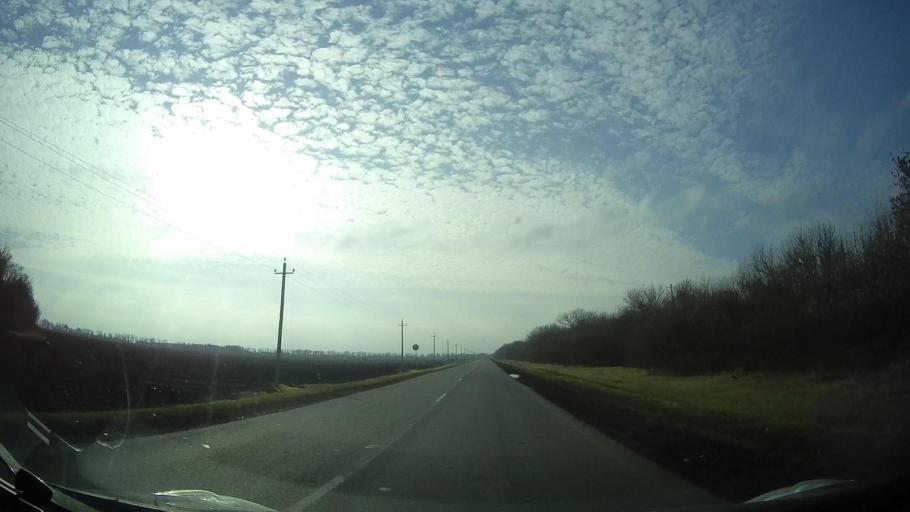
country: RU
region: Rostov
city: Mechetinskaya
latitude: 46.7984
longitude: 40.5096
